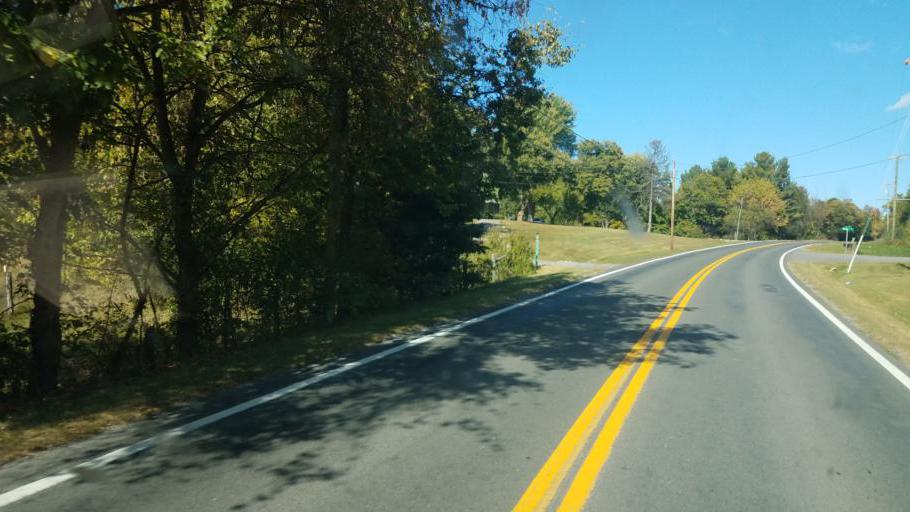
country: US
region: Virginia
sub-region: Warren County
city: Front Royal
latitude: 38.8925
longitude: -78.2397
